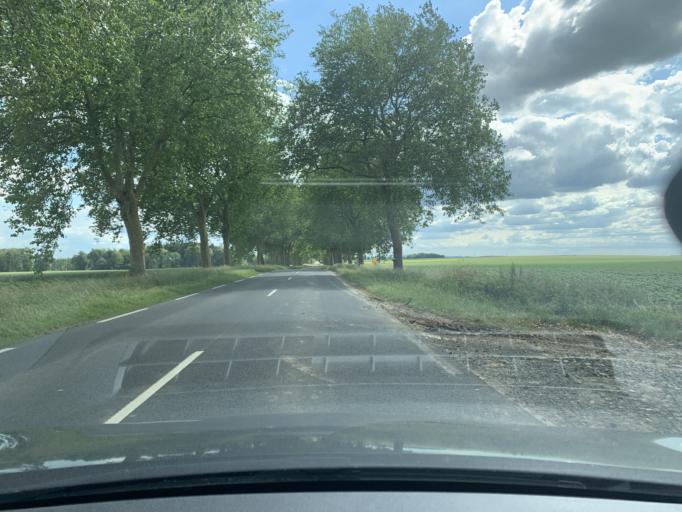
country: FR
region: Picardie
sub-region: Departement de la Somme
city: Moislains
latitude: 49.9807
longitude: 2.9988
